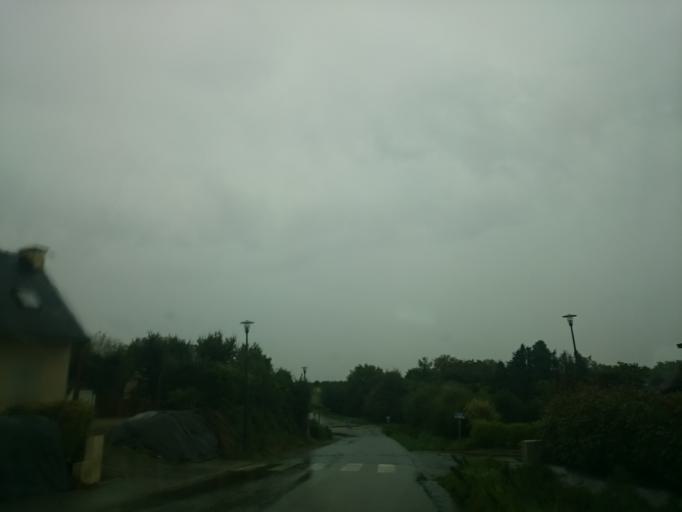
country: FR
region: Brittany
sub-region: Departement du Finistere
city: Le Drennec
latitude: 48.5358
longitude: -4.3745
